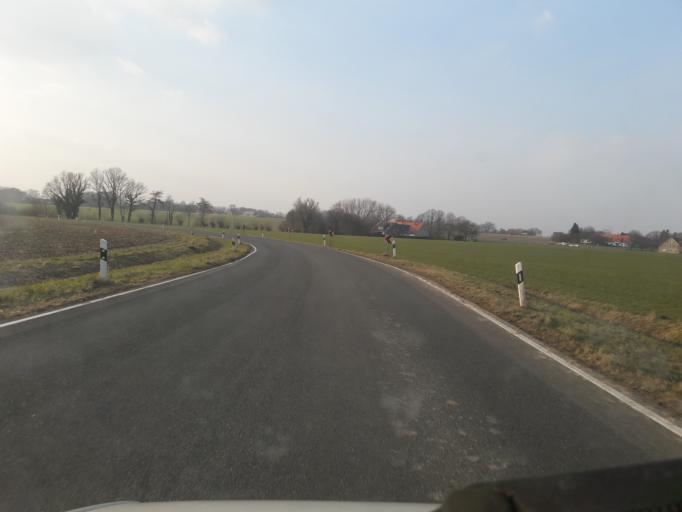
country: DE
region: North Rhine-Westphalia
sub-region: Regierungsbezirk Detmold
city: Huellhorst
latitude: 52.3365
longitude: 8.6615
